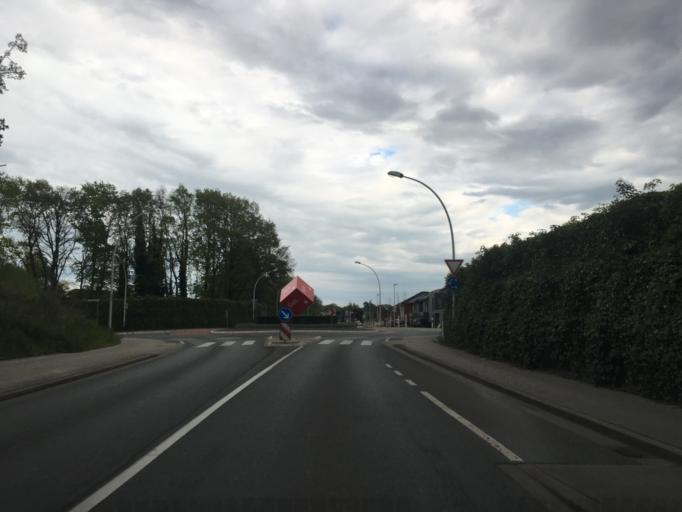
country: DE
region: North Rhine-Westphalia
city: Emsdetten
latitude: 52.1614
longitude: 7.5172
